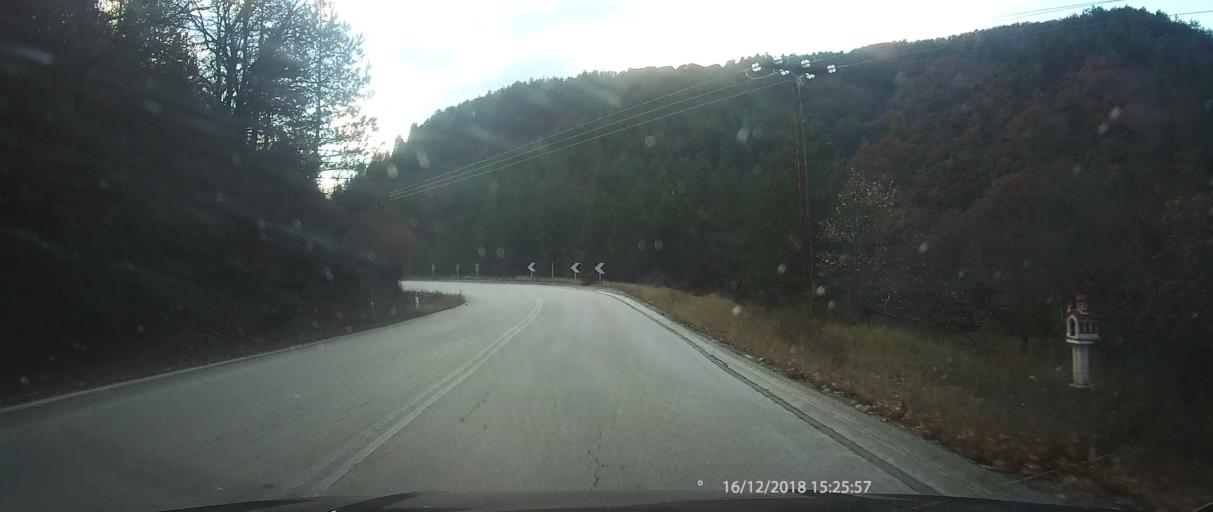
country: GR
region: Epirus
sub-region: Nomos Ioanninon
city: Konitsa
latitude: 40.1220
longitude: 20.7815
